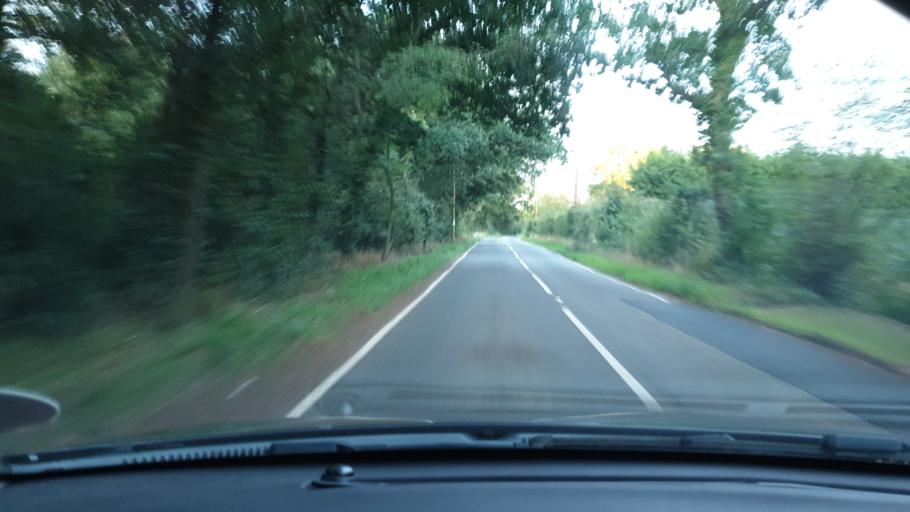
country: GB
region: England
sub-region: Essex
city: Alresford
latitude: 51.9054
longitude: 0.9890
